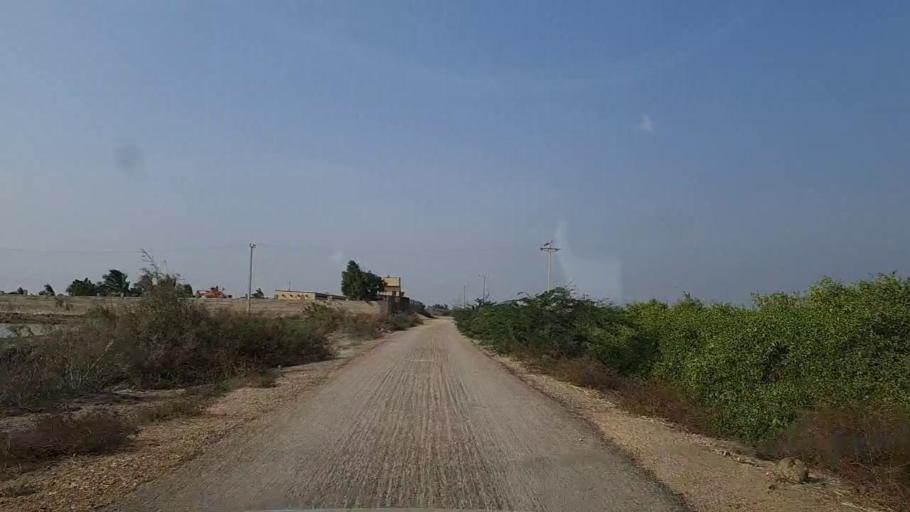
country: PK
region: Sindh
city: Mirpur Sakro
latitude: 24.5744
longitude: 67.5711
